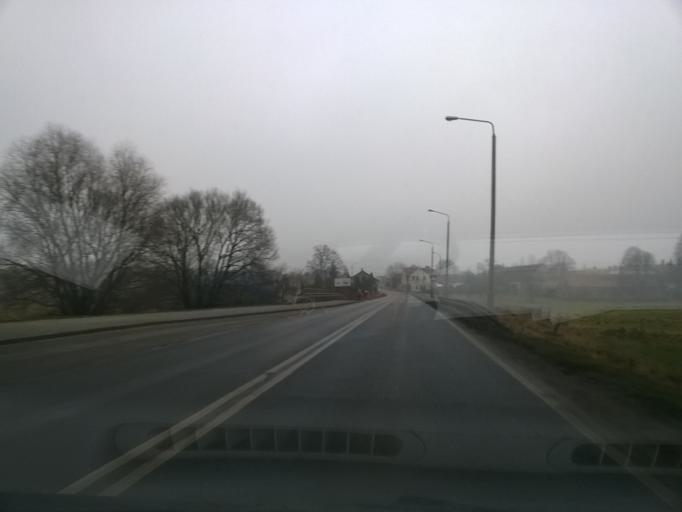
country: PL
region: Kujawsko-Pomorskie
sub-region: Powiat nakielski
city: Naklo nad Notecia
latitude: 53.1209
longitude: 17.6028
